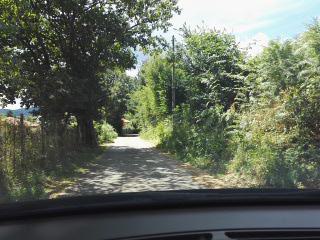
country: IT
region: Calabria
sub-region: Provincia di Vibo-Valentia
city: Serra San Bruno
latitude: 38.5770
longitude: 16.3195
